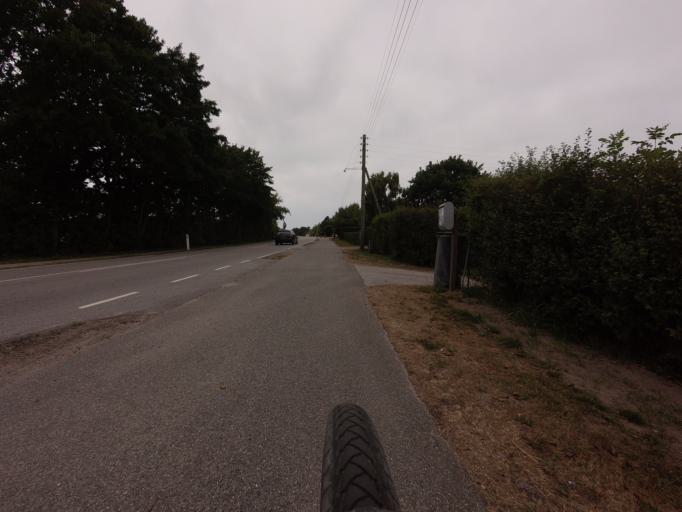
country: DK
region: North Denmark
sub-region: Laeso Kommune
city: Byrum
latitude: 57.2863
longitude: 10.9291
